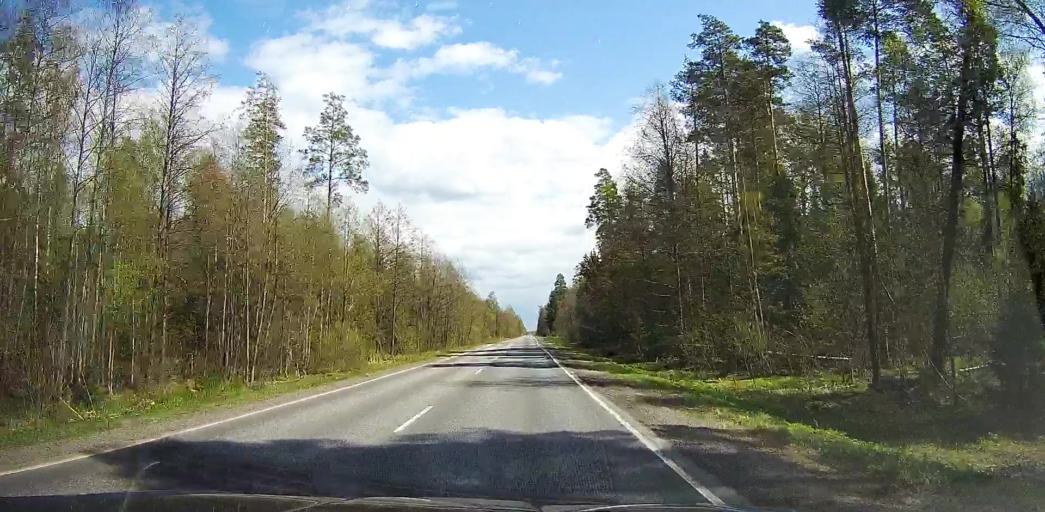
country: RU
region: Moskovskaya
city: Davydovo
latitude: 55.5514
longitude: 38.7686
